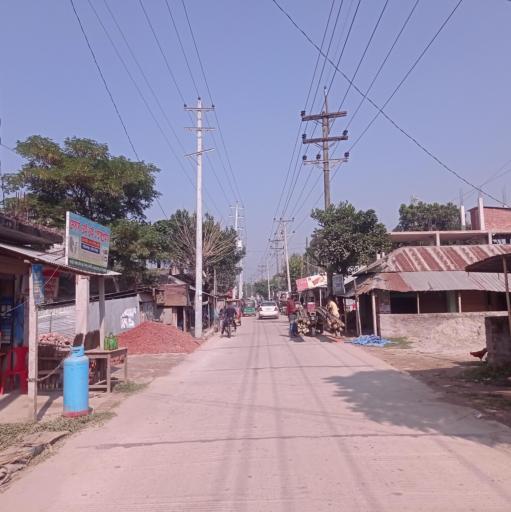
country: BD
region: Dhaka
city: Narsingdi
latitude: 24.0670
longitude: 90.6915
